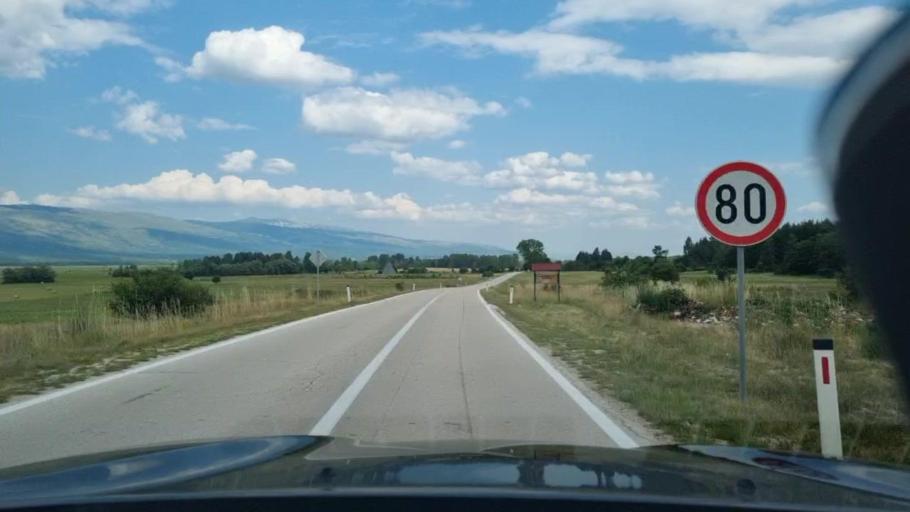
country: HR
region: Splitsko-Dalmatinska
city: Hrvace
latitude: 43.9865
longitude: 16.6301
